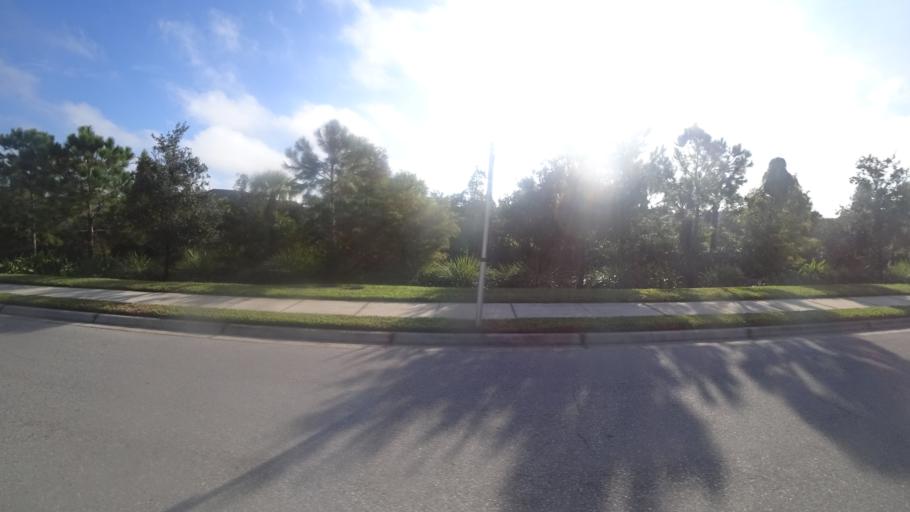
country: US
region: Florida
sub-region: Manatee County
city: Ellenton
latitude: 27.5513
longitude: -82.4527
